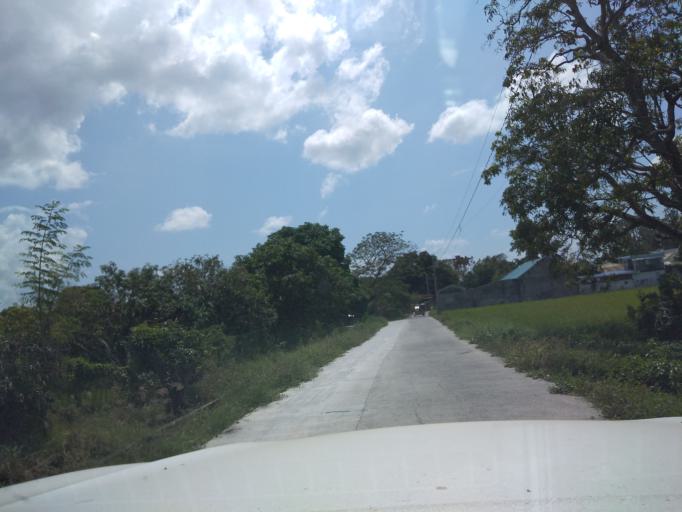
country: PH
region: Central Luzon
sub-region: Province of Pampanga
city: Lourdes
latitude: 15.0102
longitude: 120.8680
